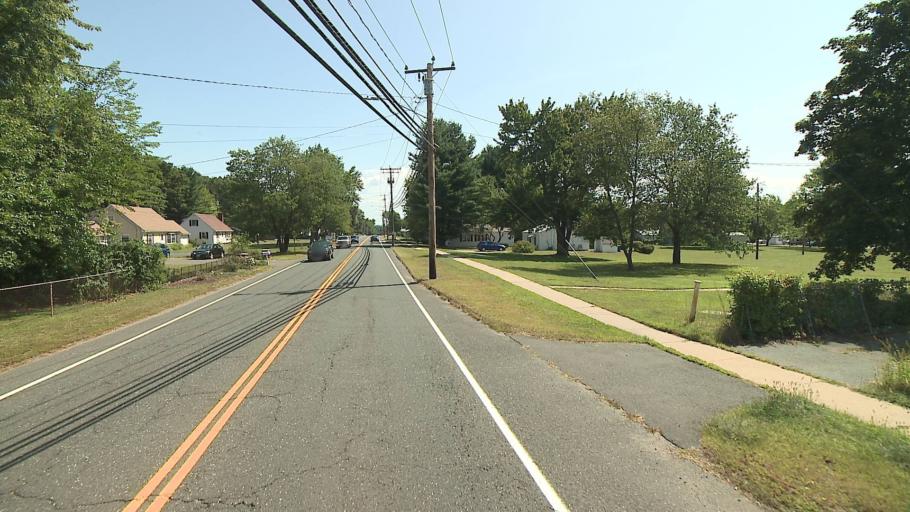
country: US
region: Connecticut
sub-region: Hartford County
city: Windsor Locks
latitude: 41.9265
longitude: -72.6518
